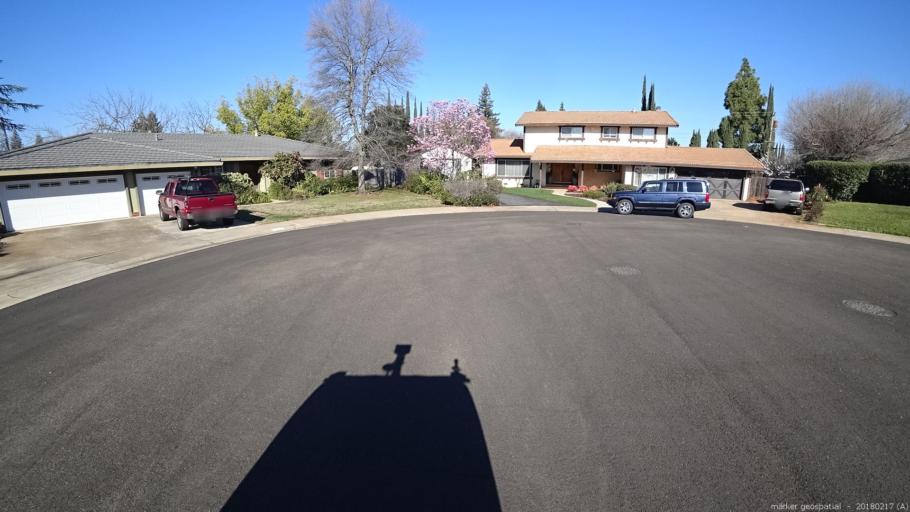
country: US
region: California
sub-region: Sacramento County
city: Folsom
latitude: 38.6614
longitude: -121.1994
